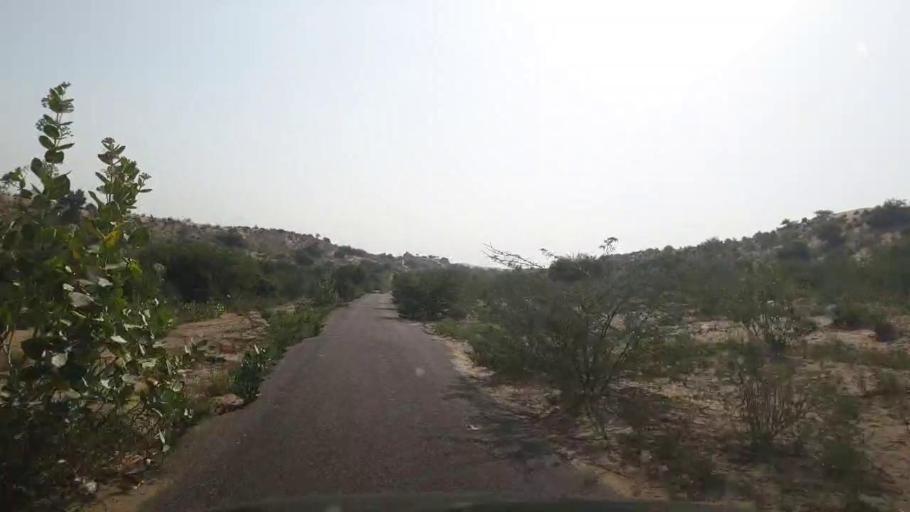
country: PK
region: Sindh
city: Islamkot
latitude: 25.1139
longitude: 70.5084
